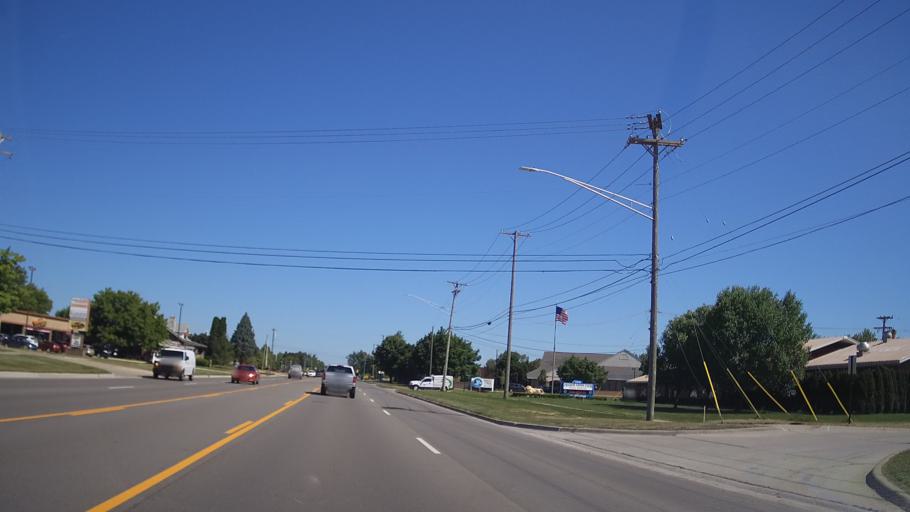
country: US
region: Michigan
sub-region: Macomb County
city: Fraser
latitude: 42.5494
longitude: -82.9588
